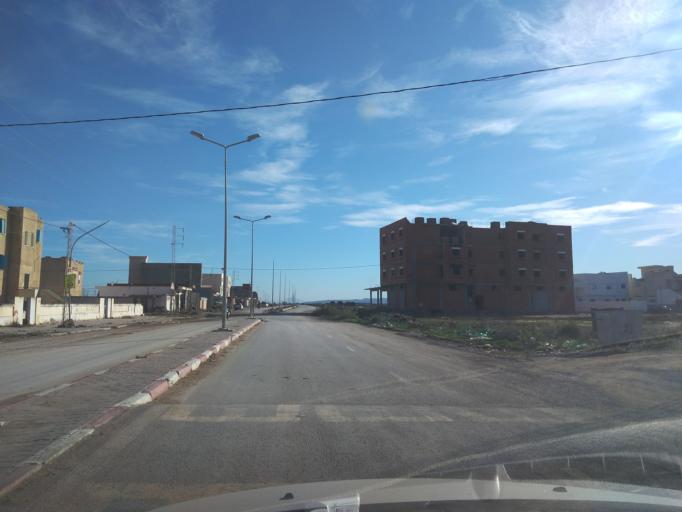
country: TN
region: Ariana
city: Qal'at al Andalus
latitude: 37.0530
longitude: 10.1221
